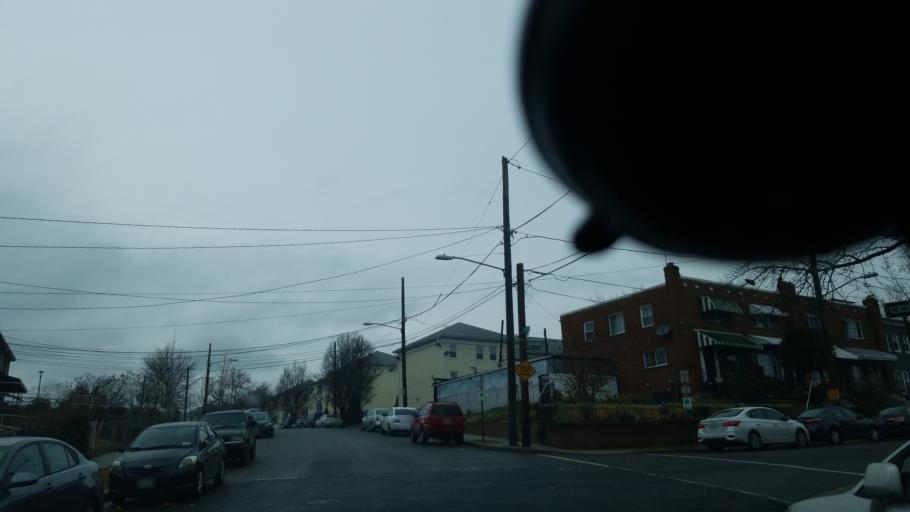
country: US
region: Maryland
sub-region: Prince George's County
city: Mount Rainier
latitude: 38.9200
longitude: -76.9821
